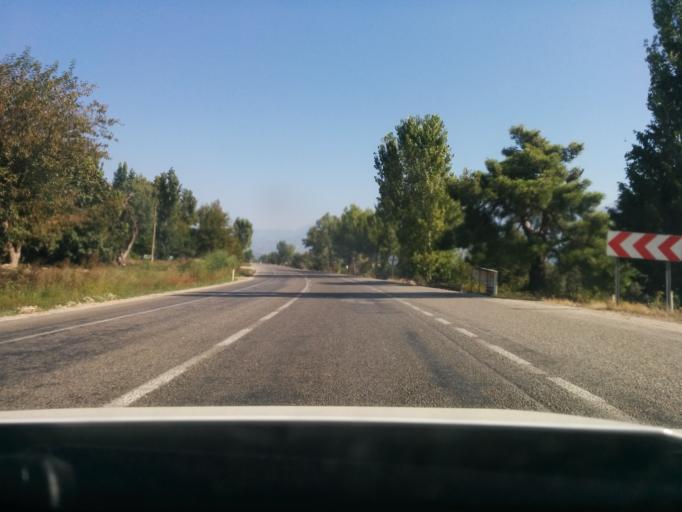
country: TR
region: Mugla
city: Esen
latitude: 36.5072
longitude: 29.3313
